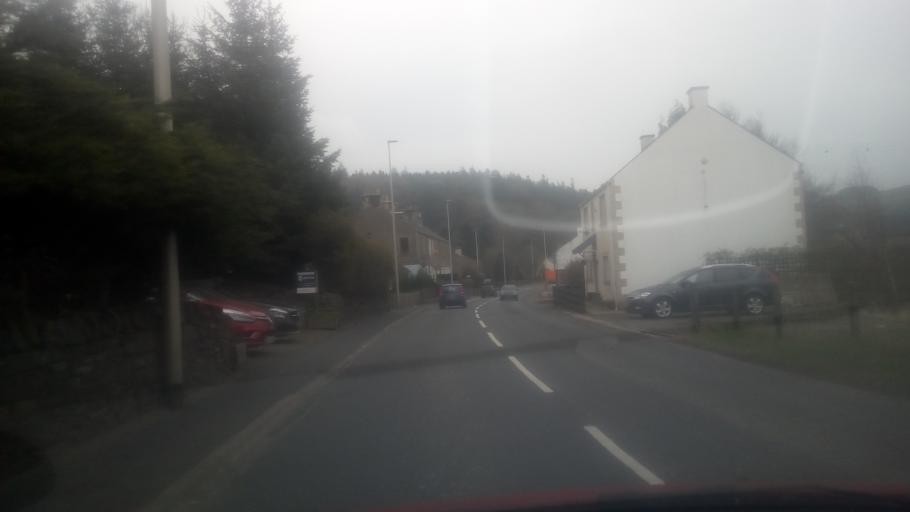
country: GB
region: Scotland
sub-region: The Scottish Borders
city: Galashiels
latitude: 55.6968
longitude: -2.8673
